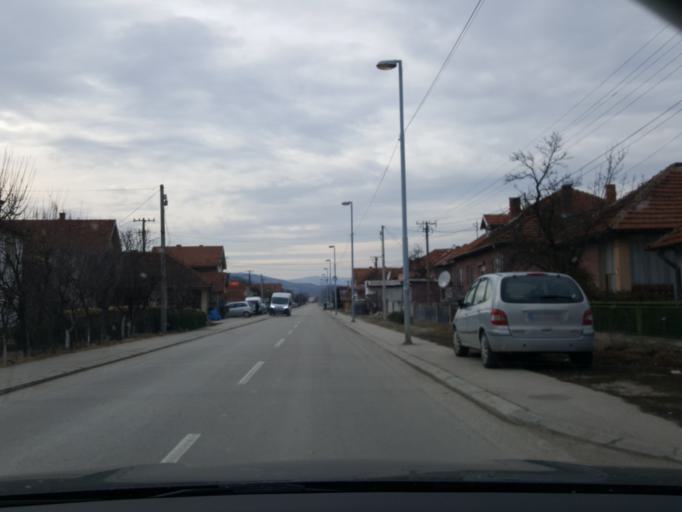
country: RS
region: Central Serbia
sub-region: Pirotski Okrug
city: Dimitrovgrad
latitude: 43.0103
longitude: 22.7589
